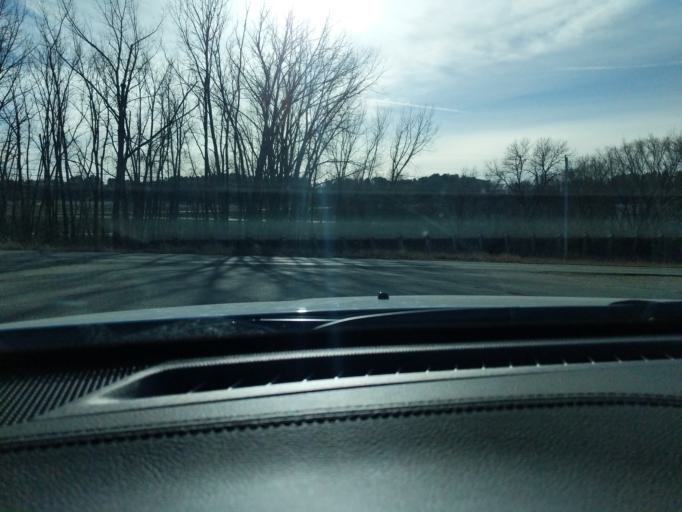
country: US
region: Minnesota
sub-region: Yellow Medicine County
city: Granite Falls
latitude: 44.8084
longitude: -95.5711
